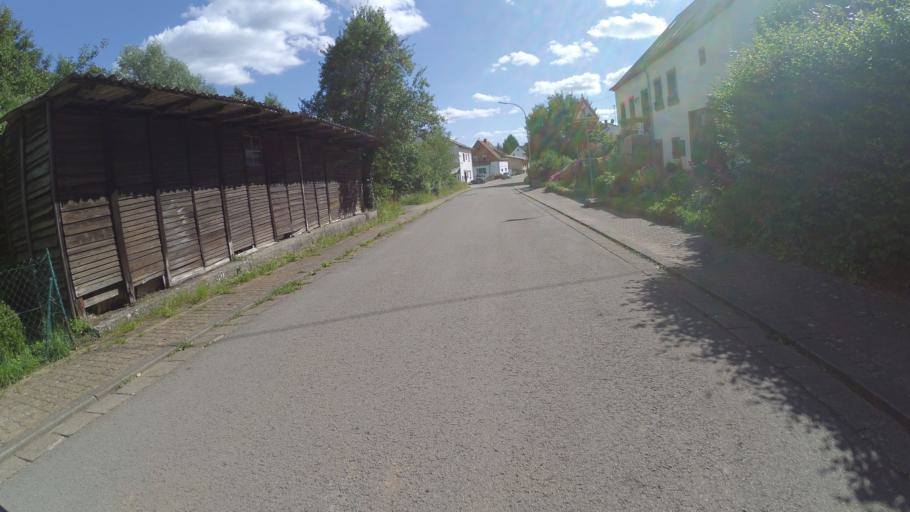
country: DE
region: Saarland
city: Marpingen
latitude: 49.4371
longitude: 7.0766
